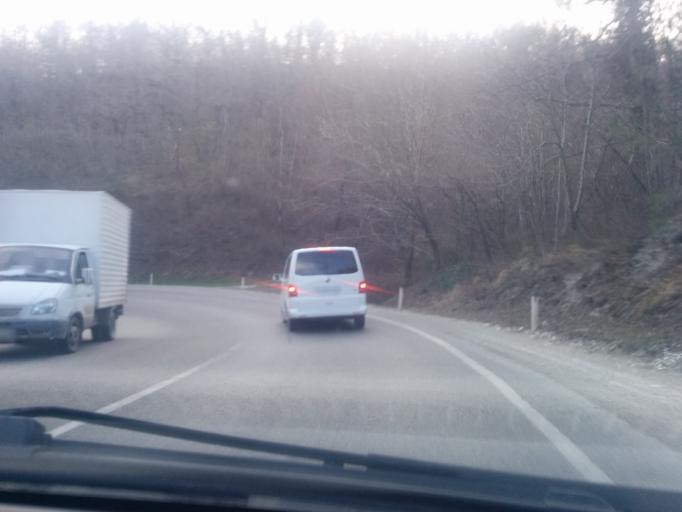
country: RU
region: Krasnodarskiy
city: Ol'ginka
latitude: 44.2432
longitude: 38.8899
